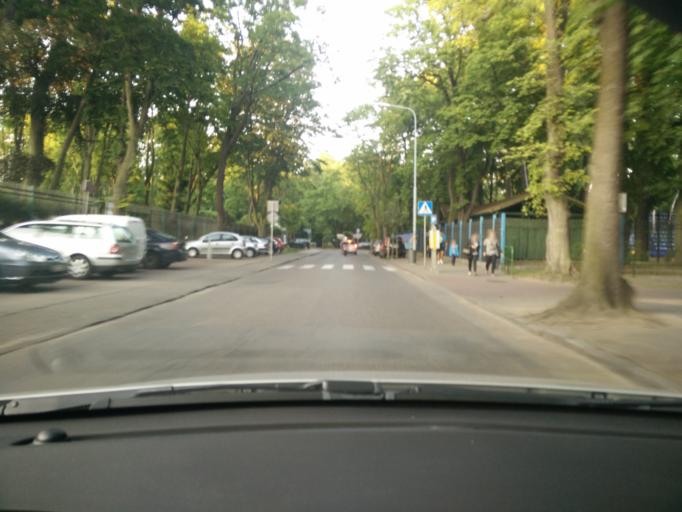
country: PL
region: Pomeranian Voivodeship
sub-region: Sopot
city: Sopot
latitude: 54.4491
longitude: 18.5639
